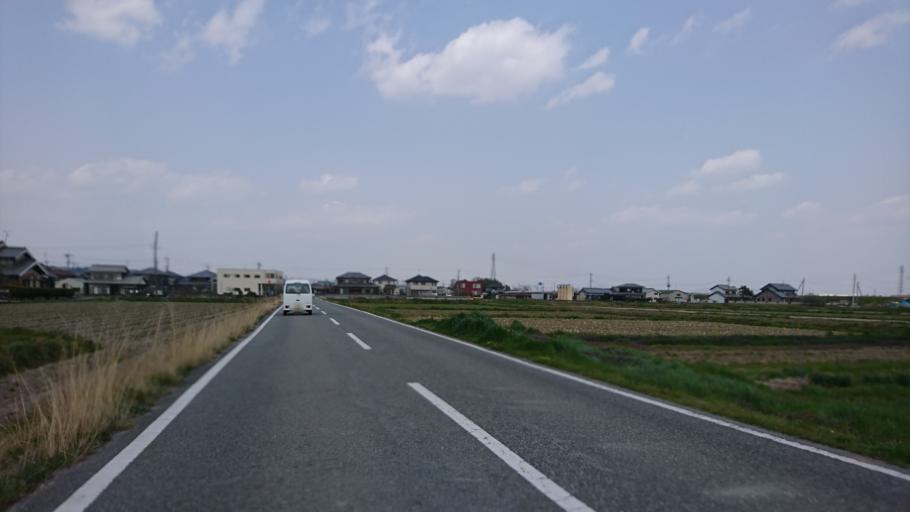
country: JP
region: Hyogo
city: Ono
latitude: 34.8585
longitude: 134.9120
